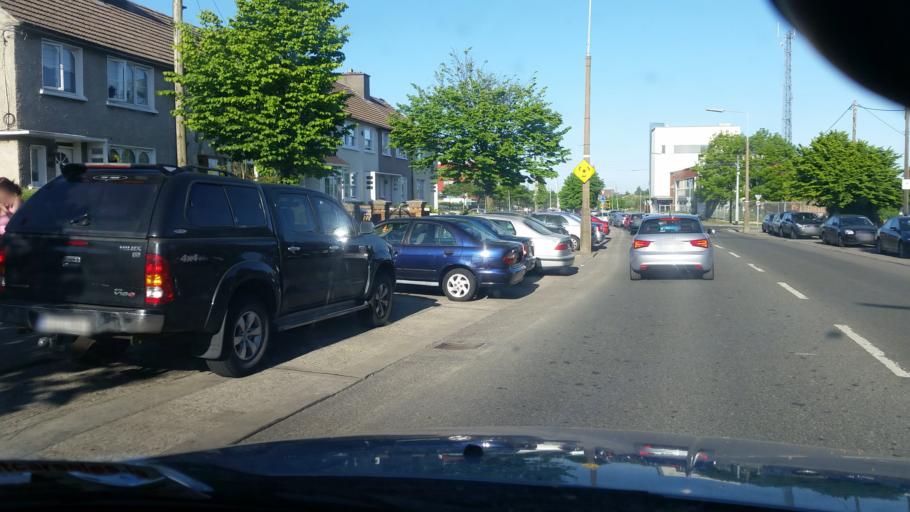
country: IE
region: Leinster
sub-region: Dublin City
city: Finglas
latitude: 53.3899
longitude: -6.3091
